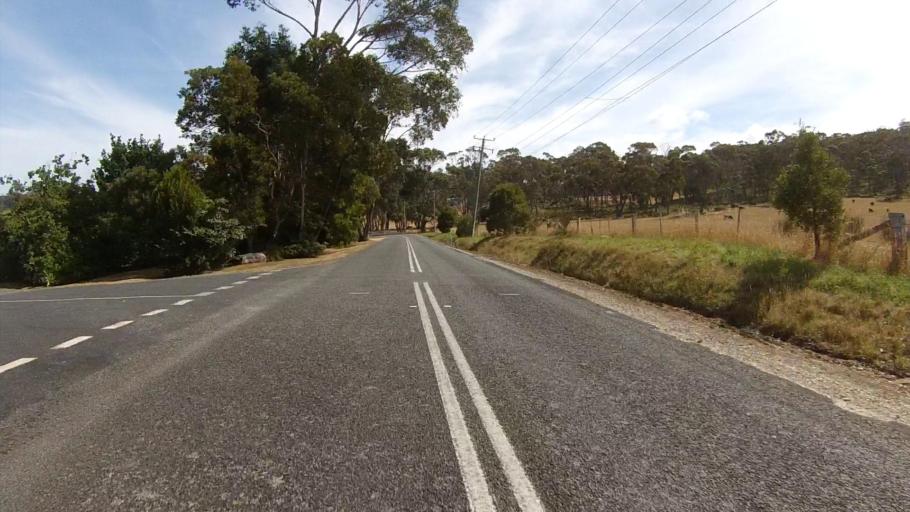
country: AU
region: Tasmania
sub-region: Huon Valley
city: Cygnet
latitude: -43.2770
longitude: 147.1626
